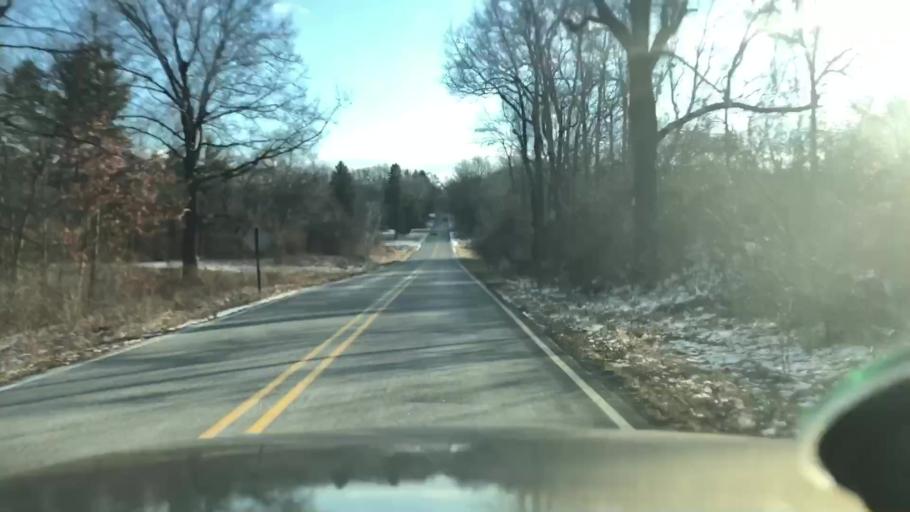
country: US
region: Michigan
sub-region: Jackson County
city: Vandercook Lake
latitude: 42.1581
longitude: -84.4521
